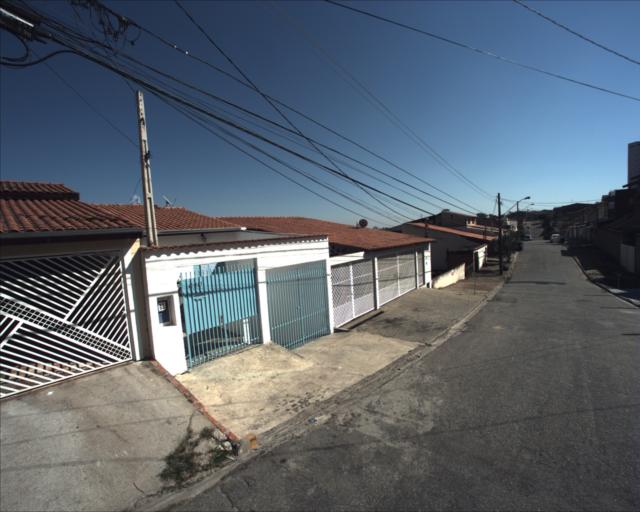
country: BR
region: Sao Paulo
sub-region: Sorocaba
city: Sorocaba
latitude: -23.5093
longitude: -47.4278
